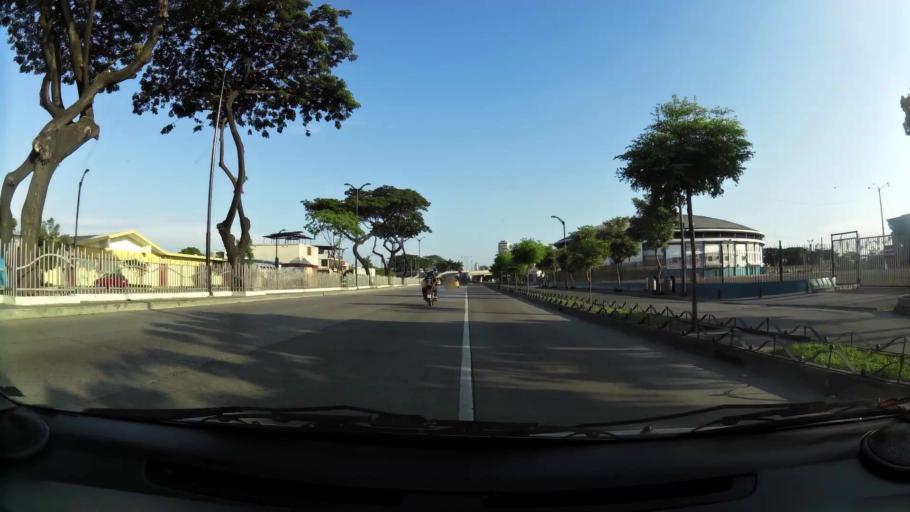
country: EC
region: Guayas
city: Guayaquil
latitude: -2.1791
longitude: -79.8923
